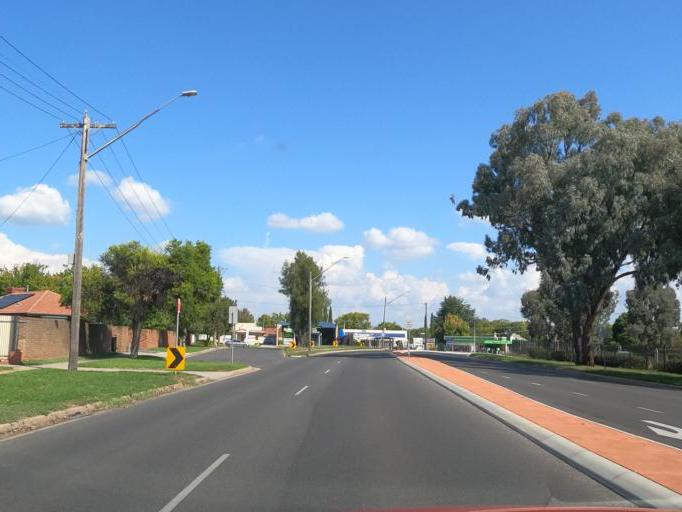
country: AU
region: New South Wales
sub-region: Albury Municipality
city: North Albury
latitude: -36.0625
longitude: 146.9262
